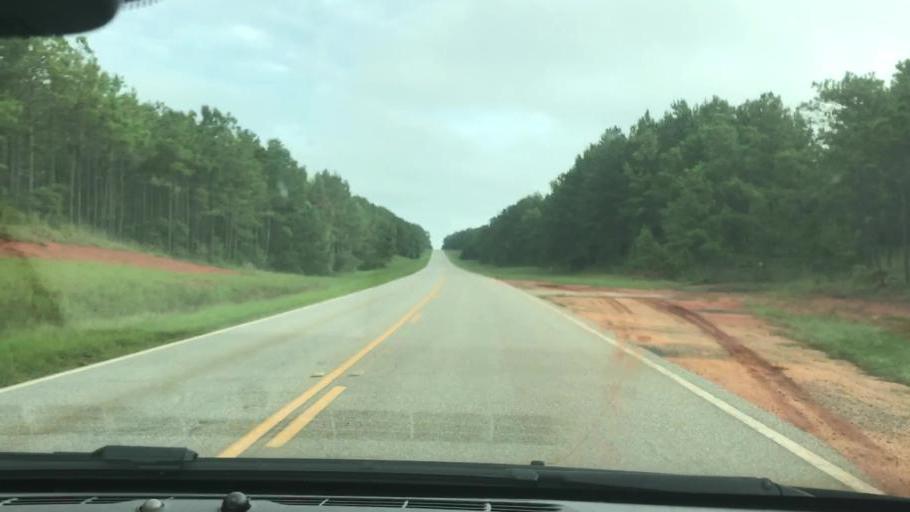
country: US
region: Georgia
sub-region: Stewart County
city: Lumpkin
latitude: 31.9931
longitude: -84.9331
